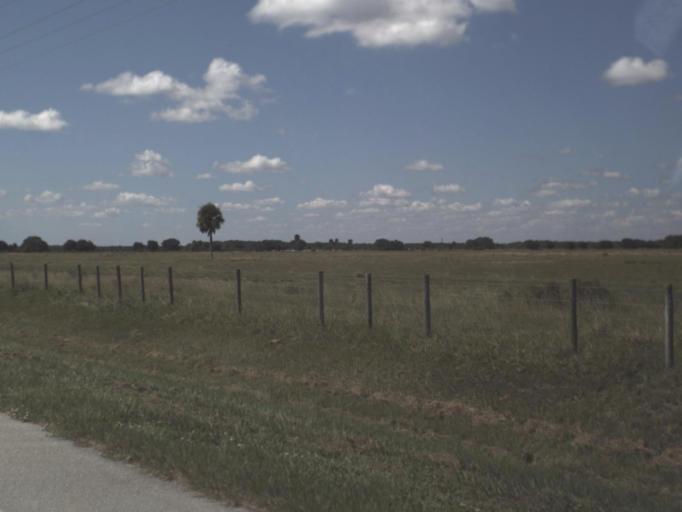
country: US
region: Florida
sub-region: Glades County
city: Moore Haven
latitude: 26.8124
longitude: -81.2534
